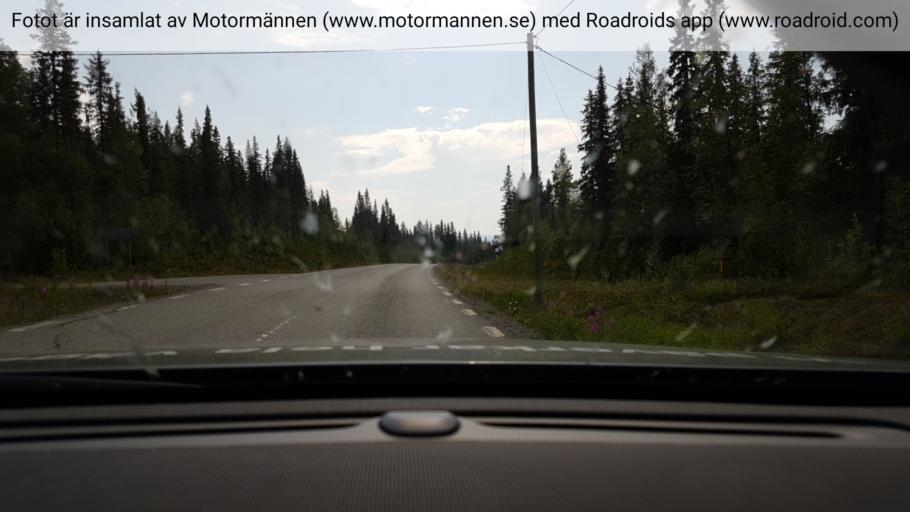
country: SE
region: Vaesterbotten
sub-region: Vilhelmina Kommun
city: Sjoberg
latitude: 65.4501
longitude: 16.1005
